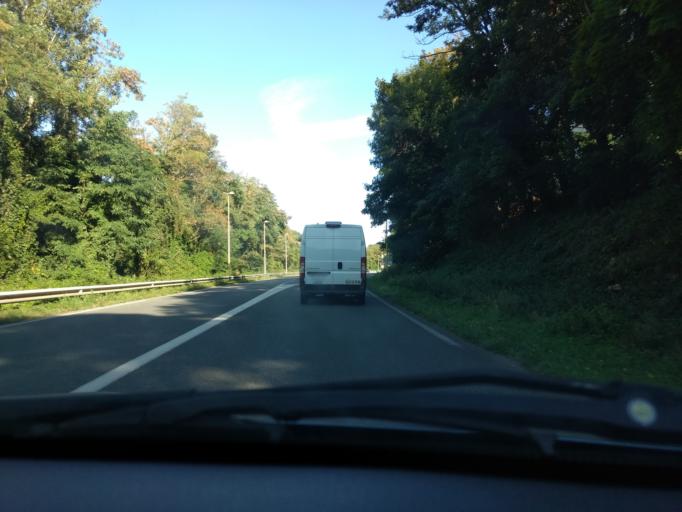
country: FR
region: Midi-Pyrenees
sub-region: Departement de l'Aveyron
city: Decazeville
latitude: 44.5586
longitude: 2.2747
